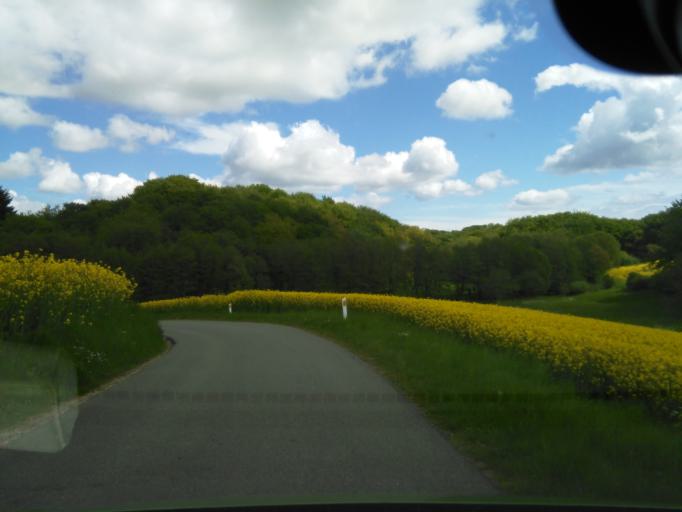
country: DK
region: Central Jutland
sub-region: Odder Kommune
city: Odder
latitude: 56.0029
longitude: 10.1238
